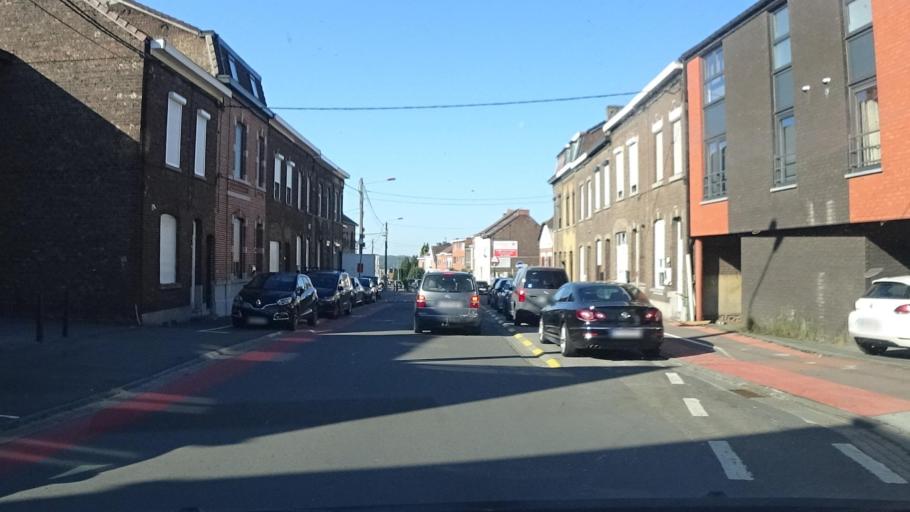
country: BE
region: Wallonia
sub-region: Province du Hainaut
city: La Louviere
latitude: 50.4659
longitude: 4.1798
